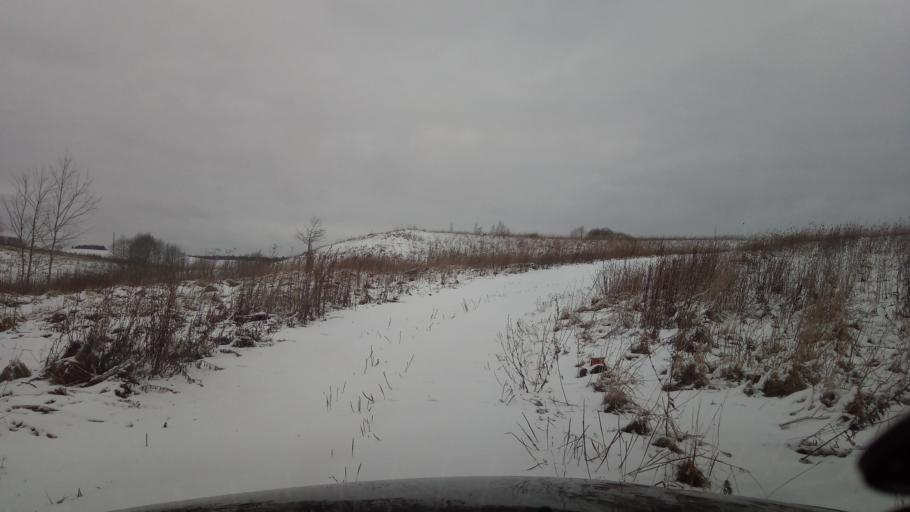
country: LT
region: Utenos apskritis
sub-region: Utena
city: Utena
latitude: 55.6086
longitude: 25.8666
